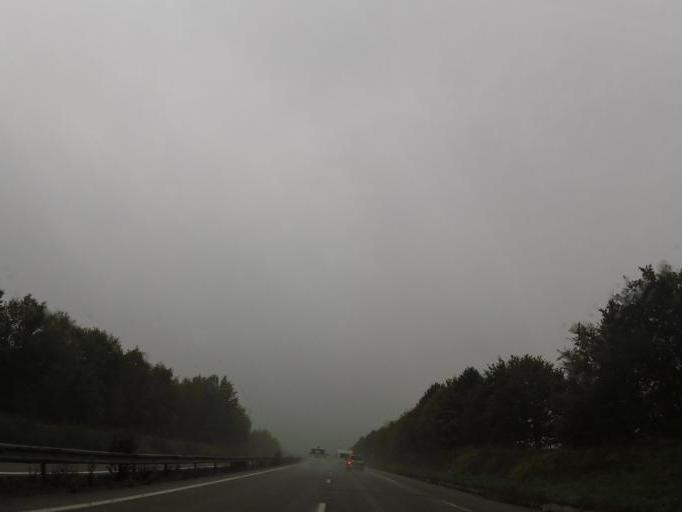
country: FR
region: Picardie
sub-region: Departement de l'Aisne
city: Brasles
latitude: 49.0920
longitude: 3.4272
